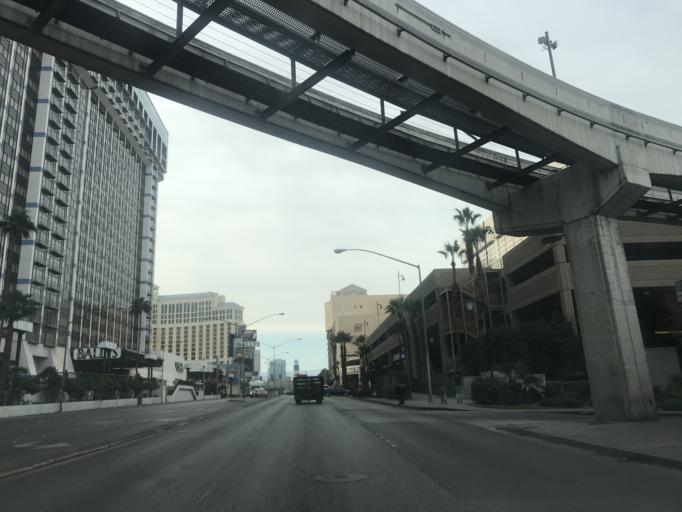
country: US
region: Nevada
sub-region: Clark County
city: Paradise
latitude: 36.1146
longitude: -115.1684
